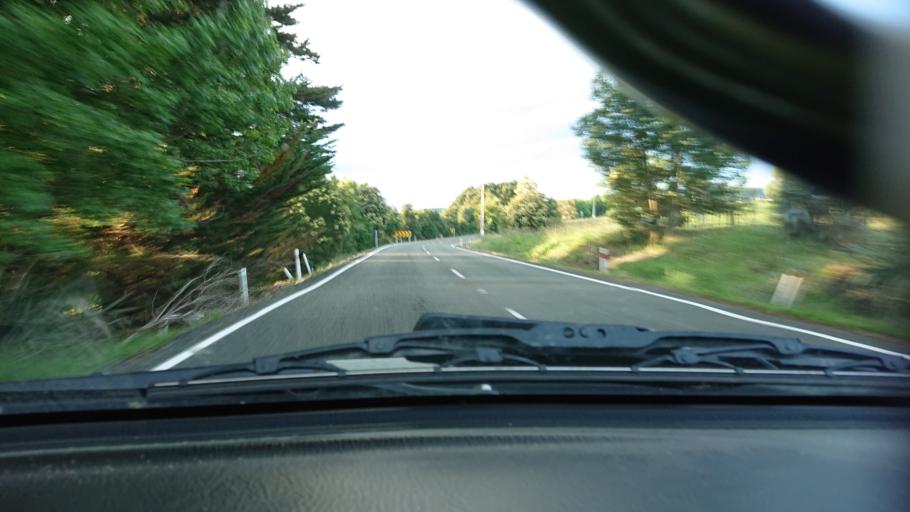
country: NZ
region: Auckland
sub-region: Auckland
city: Parakai
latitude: -36.5224
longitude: 174.4492
